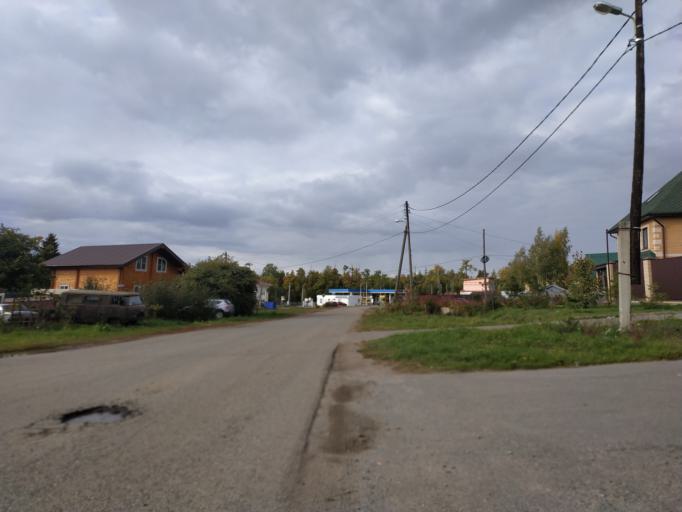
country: RU
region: Chuvashia
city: Ishley
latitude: 56.1316
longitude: 47.0873
